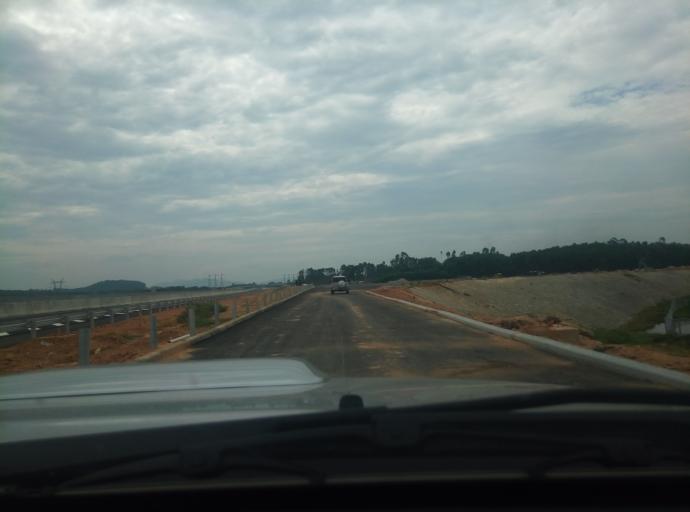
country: VN
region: Quang Nam
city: Tam Ky
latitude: 15.5283
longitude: 108.4795
